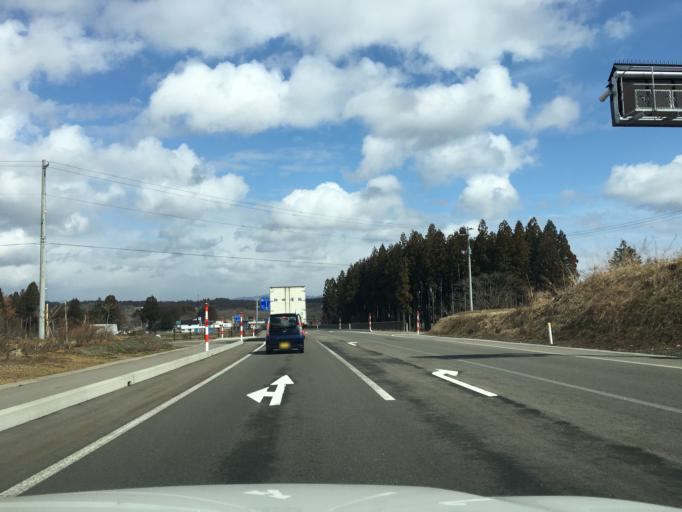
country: JP
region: Akita
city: Takanosu
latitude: 40.1159
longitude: 140.3763
